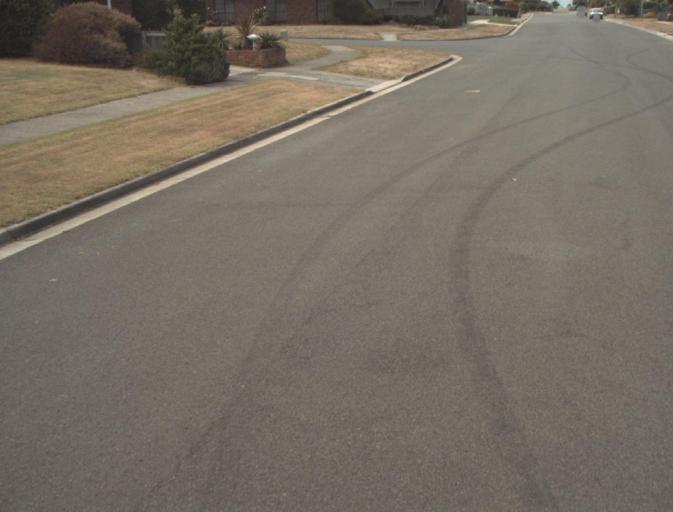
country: AU
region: Tasmania
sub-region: Launceston
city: Invermay
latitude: -41.3910
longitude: 147.1150
